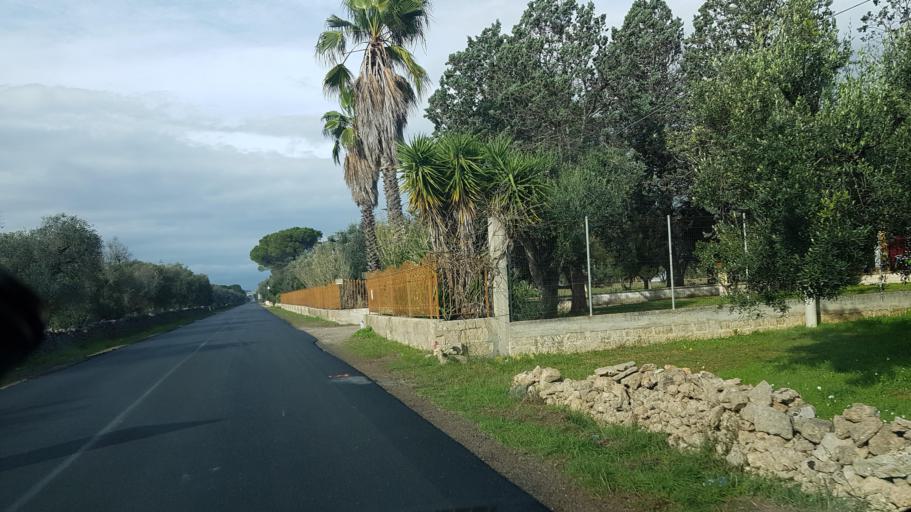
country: IT
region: Apulia
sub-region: Provincia di Brindisi
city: Oria
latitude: 40.4816
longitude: 17.6855
